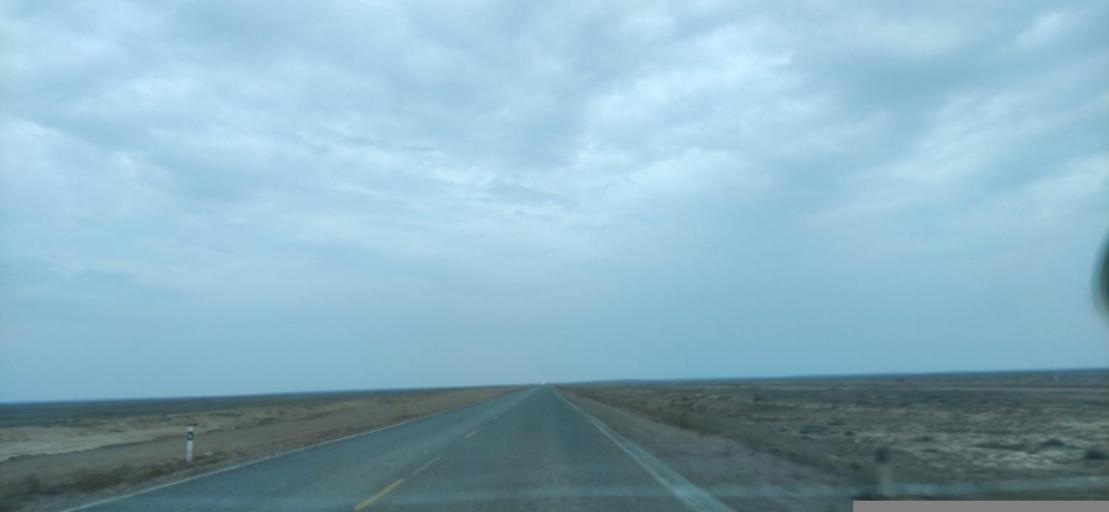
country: KZ
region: Qaraghandy
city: Saryshaghan
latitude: 46.2482
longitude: 73.6776
